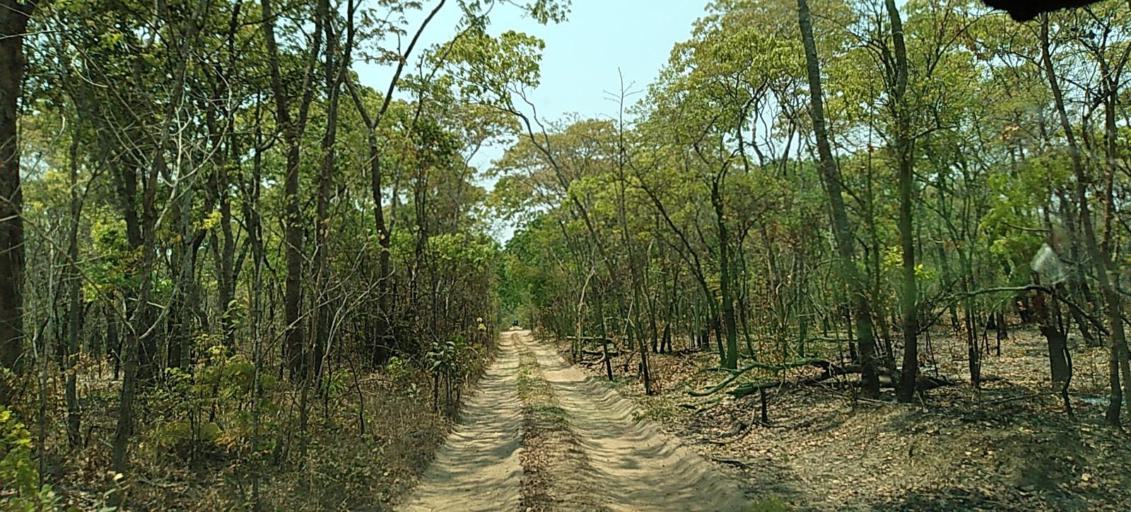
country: ZM
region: North-Western
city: Kabompo
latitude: -13.6462
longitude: 24.4822
